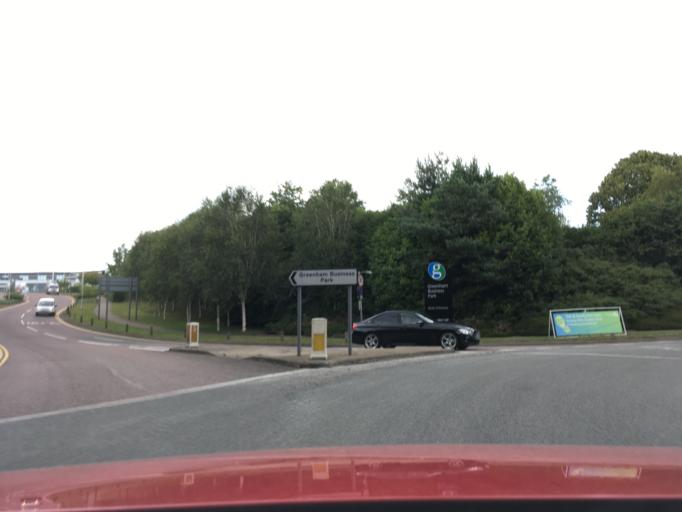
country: GB
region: England
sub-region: West Berkshire
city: Greenham
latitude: 51.3720
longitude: -1.2846
